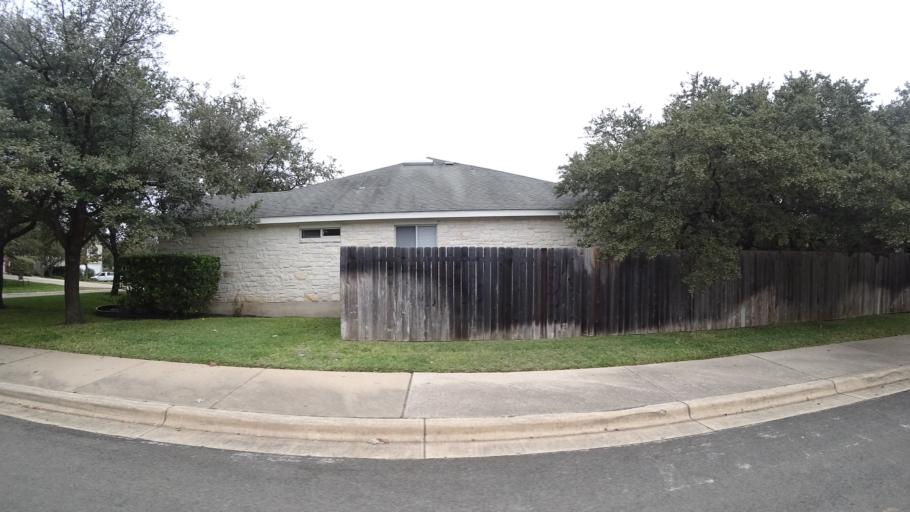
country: US
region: Texas
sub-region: Travis County
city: Shady Hollow
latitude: 30.2137
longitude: -97.8868
